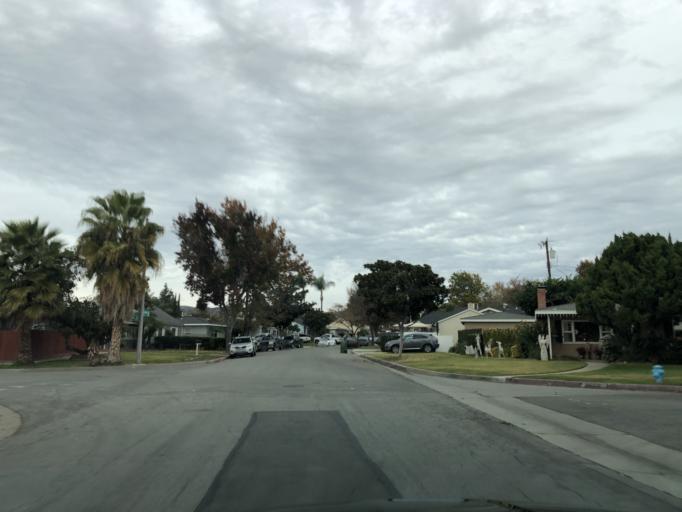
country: US
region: California
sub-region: Los Angeles County
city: South Whittier
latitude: 33.9530
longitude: -118.0233
